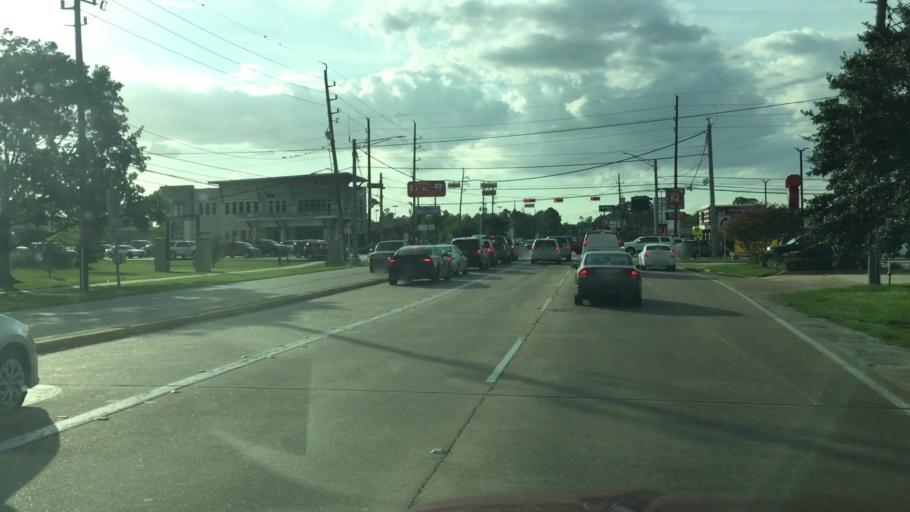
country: US
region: Texas
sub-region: Harris County
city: Hudson
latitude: 30.0205
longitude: -95.5231
